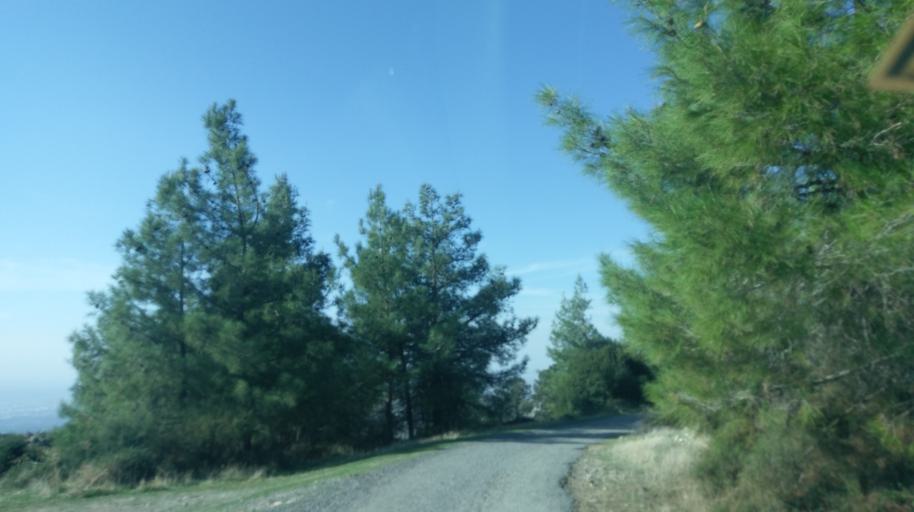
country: CY
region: Keryneia
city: Kyrenia
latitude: 35.2837
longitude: 33.4035
